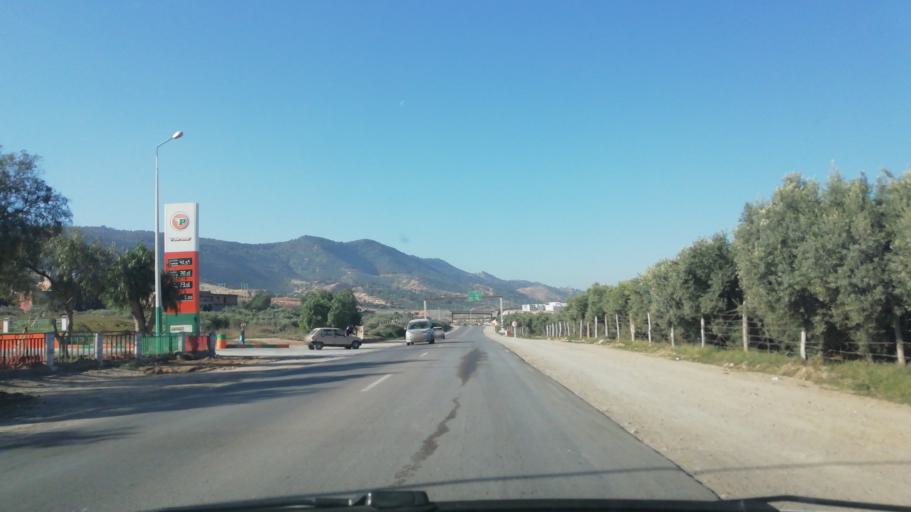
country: DZ
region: Mascara
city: Sig
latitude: 35.5322
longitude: -0.1456
